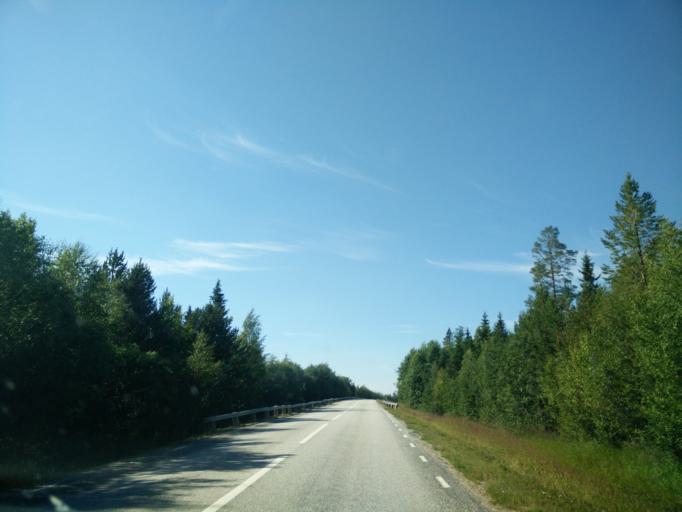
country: SE
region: Jaemtland
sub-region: Are Kommun
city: Jarpen
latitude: 62.7999
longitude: 13.5693
